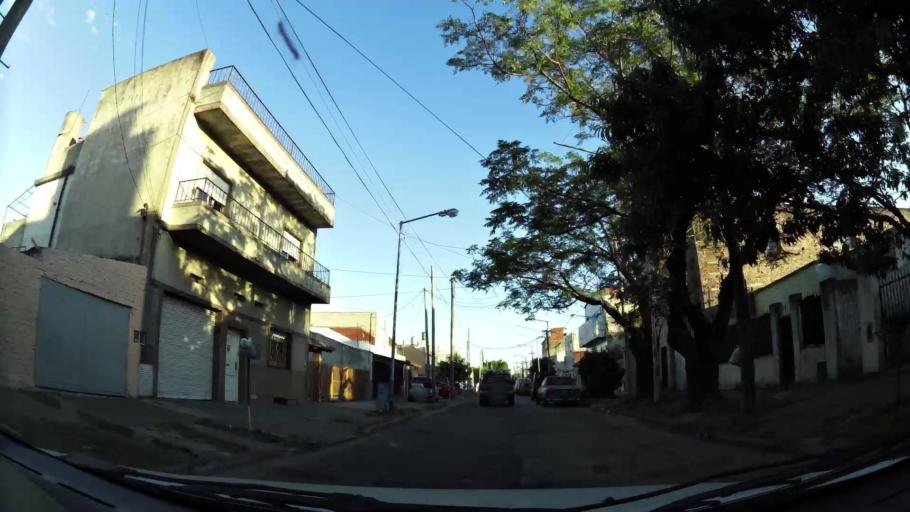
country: AR
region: Buenos Aires
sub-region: Partido de General San Martin
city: General San Martin
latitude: -34.5639
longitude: -58.5287
